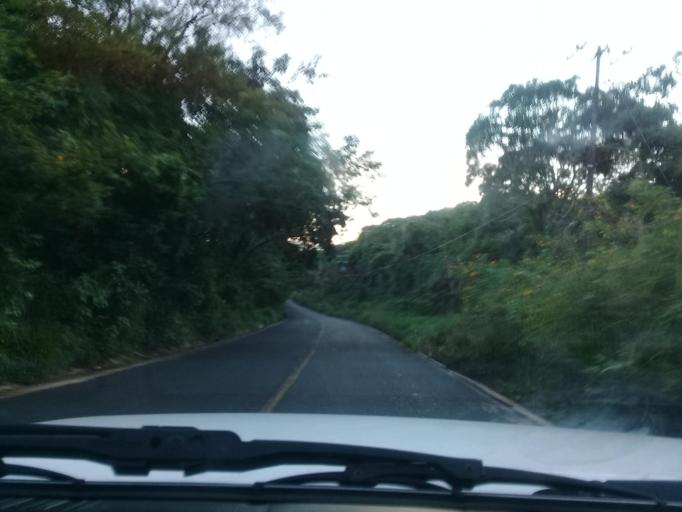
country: MX
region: Veracruz
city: Catemaco
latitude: 18.4351
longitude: -95.0903
